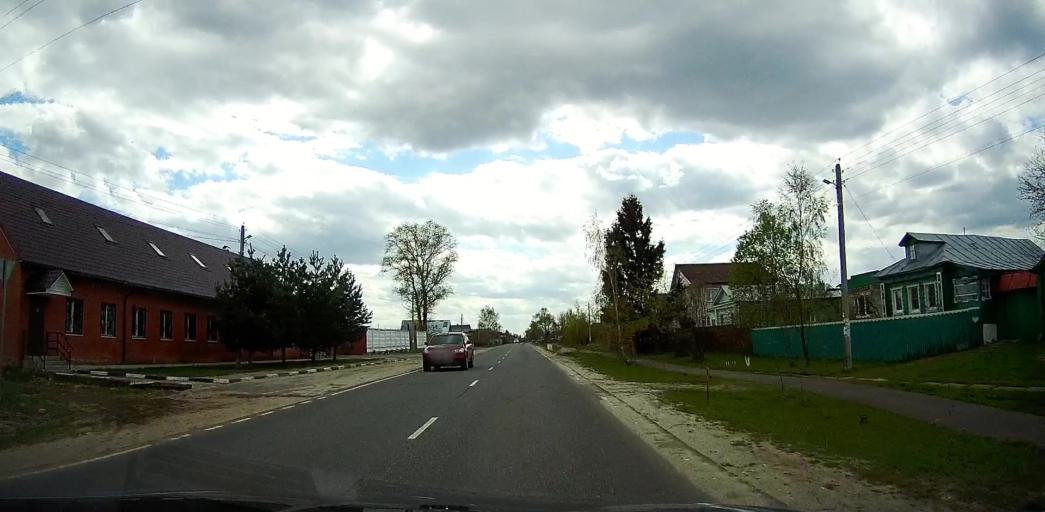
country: RU
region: Moskovskaya
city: Drezna
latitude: 55.6689
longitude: 38.7643
